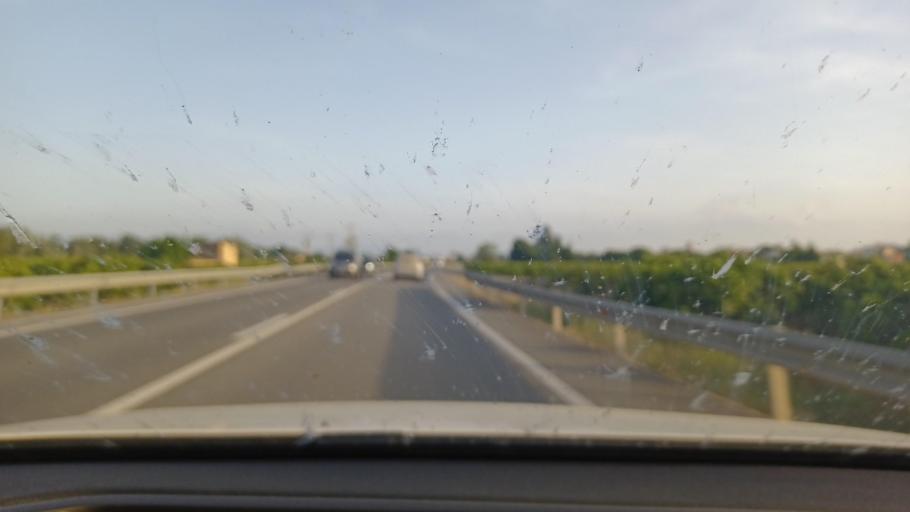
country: ES
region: Catalonia
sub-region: Provincia de Tarragona
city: Tortosa
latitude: 40.8330
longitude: 0.5151
